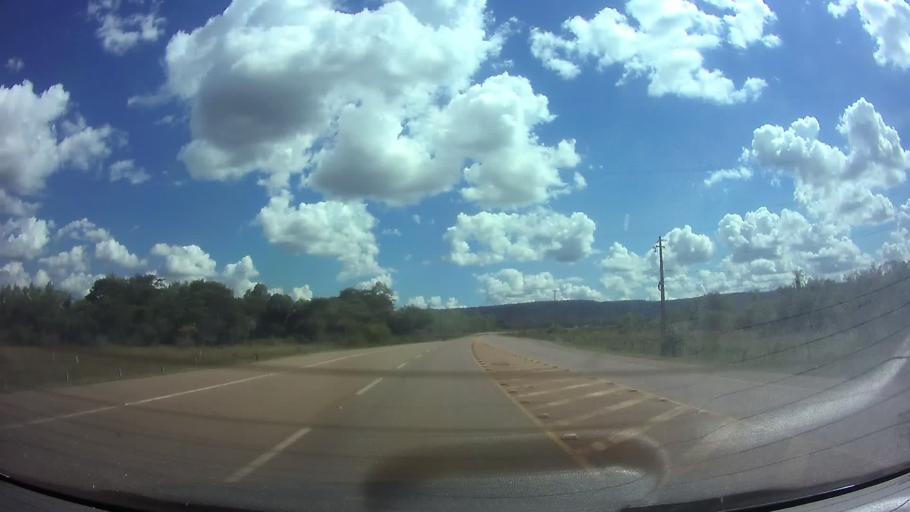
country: PY
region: Guaira
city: Itape
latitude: -25.9100
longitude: -56.6758
